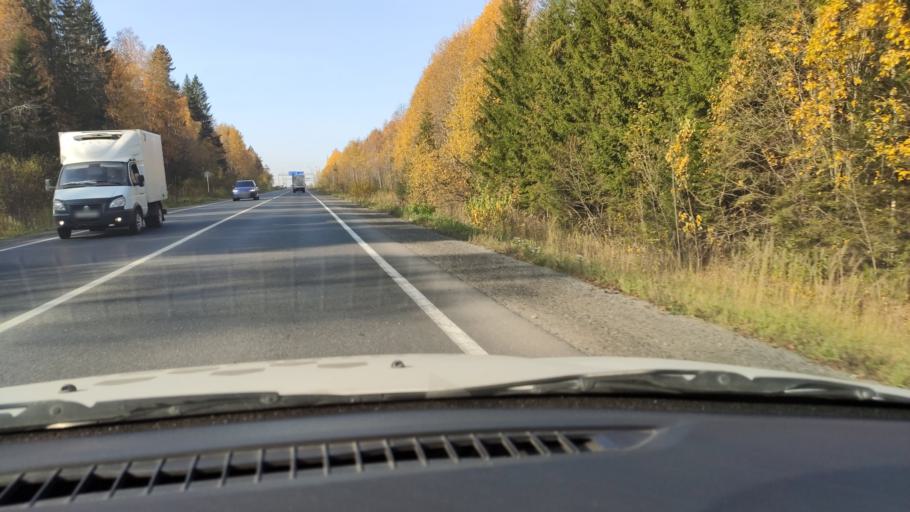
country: RU
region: Perm
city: Novyye Lyady
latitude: 58.0433
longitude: 56.4438
